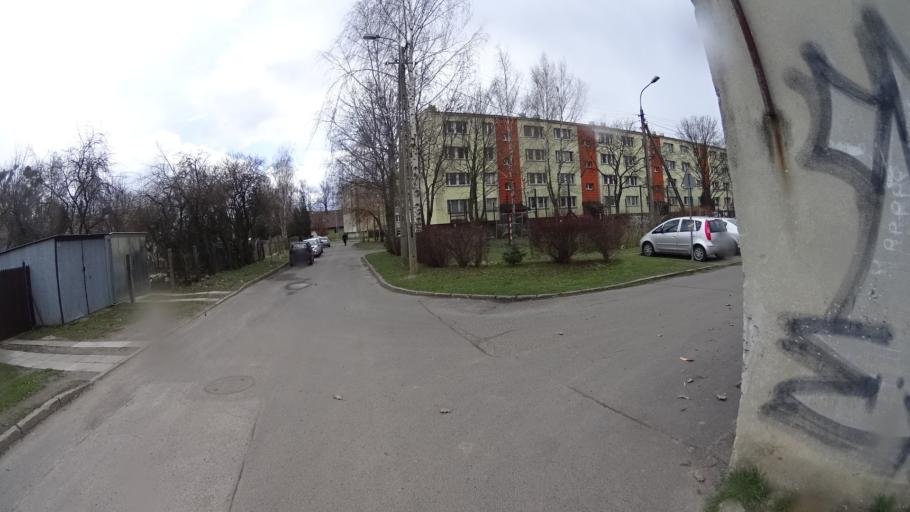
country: PL
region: Masovian Voivodeship
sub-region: Powiat warszawski zachodni
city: Blonie
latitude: 52.2173
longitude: 20.6472
